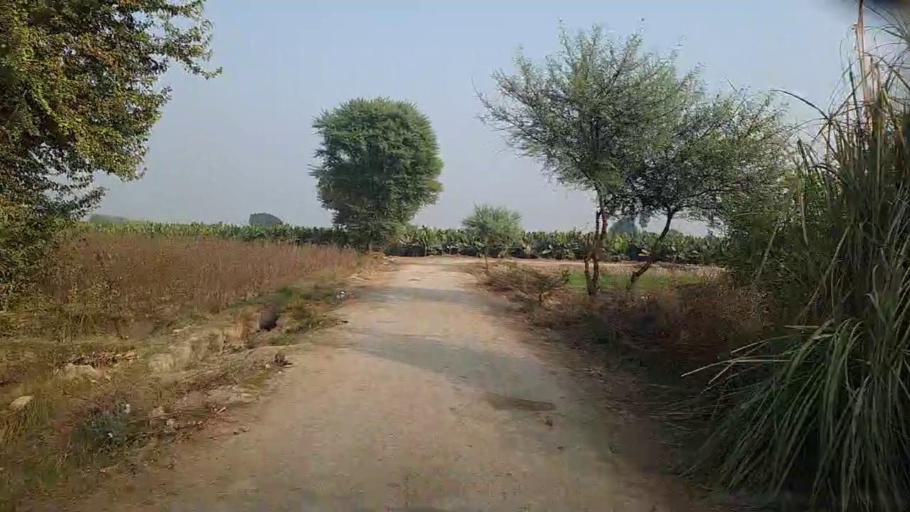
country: PK
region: Sindh
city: Kandiari
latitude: 27.0087
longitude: 68.4945
